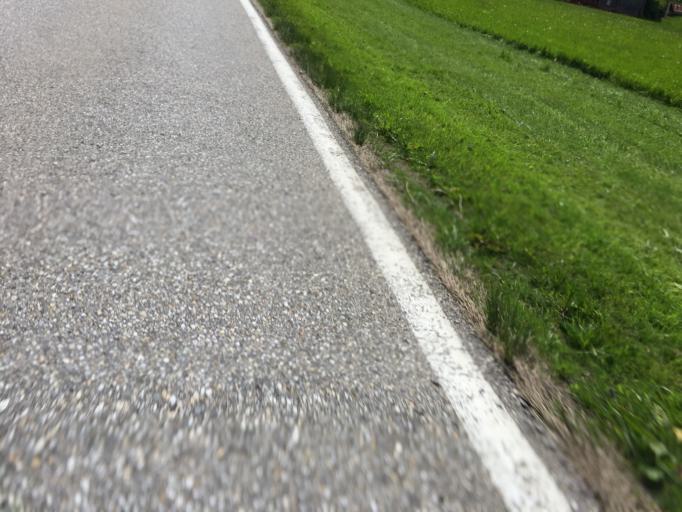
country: CH
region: Lucerne
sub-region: Entlebuch District
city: Escholzmatt
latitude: 46.9023
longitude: 7.8954
